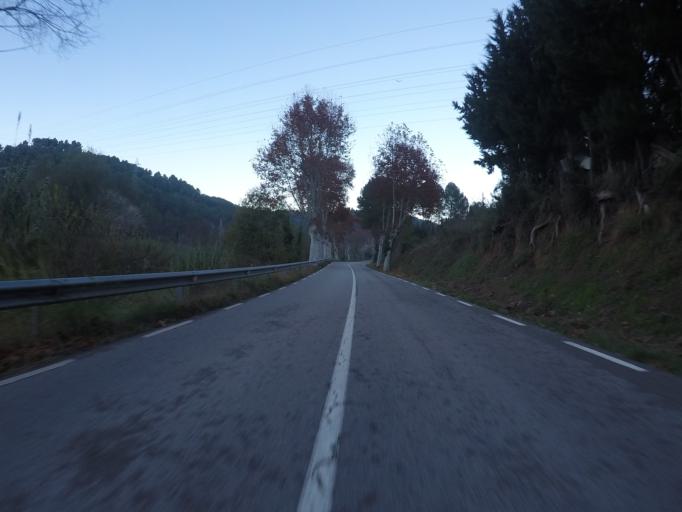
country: ES
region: Catalonia
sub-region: Provincia de Barcelona
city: Monistrol de Montserrat
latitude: 41.6174
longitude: 1.8526
